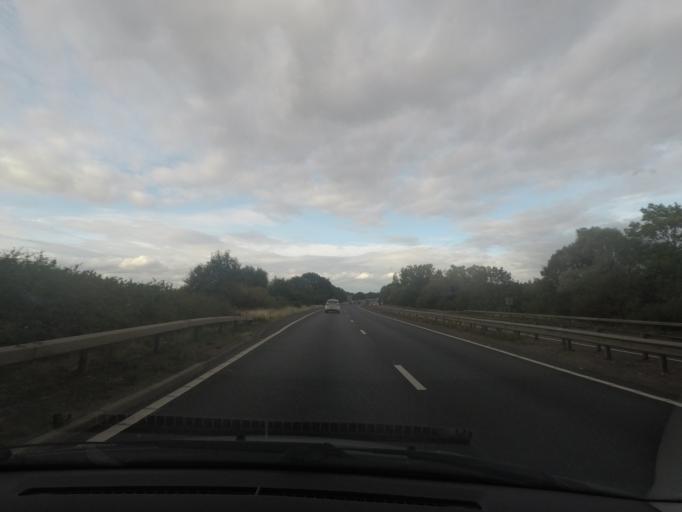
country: GB
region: England
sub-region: Oxfordshire
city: Yarnton
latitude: 51.7815
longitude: -1.3029
